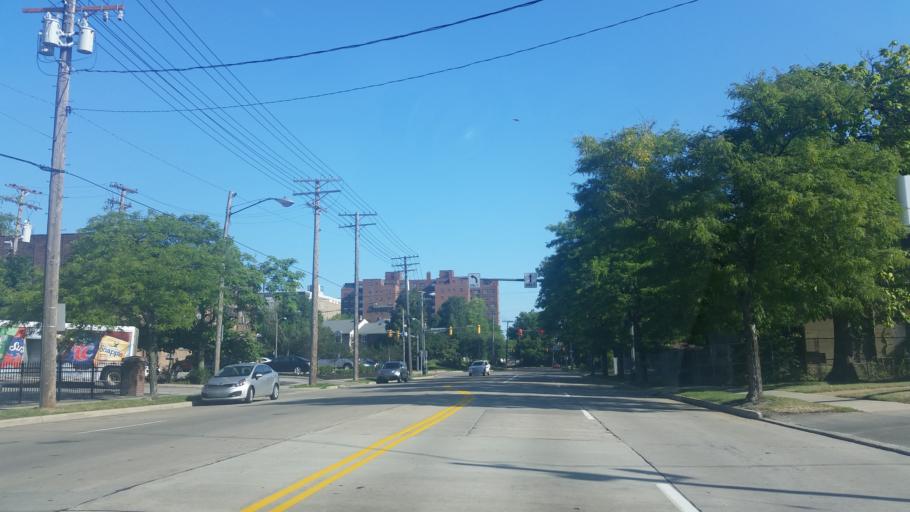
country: US
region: Ohio
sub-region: Cuyahoga County
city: Lakewood
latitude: 41.4879
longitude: -81.7687
